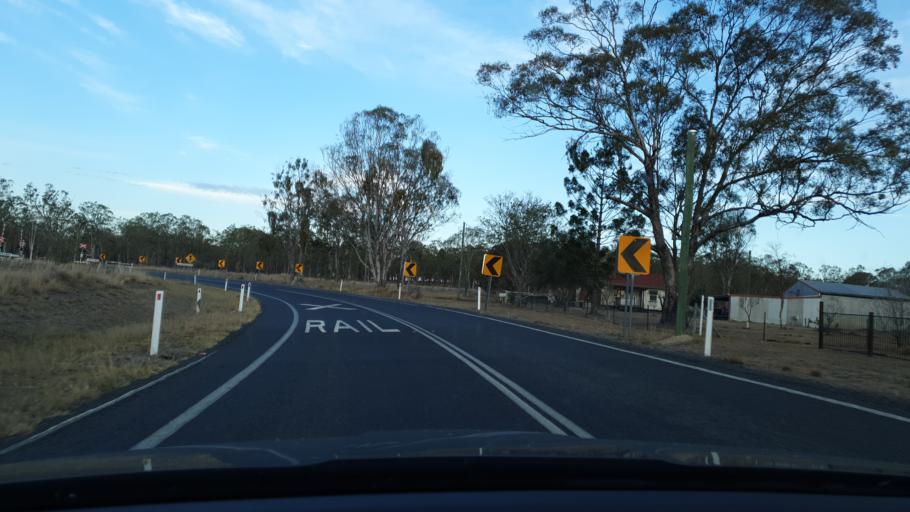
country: AU
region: Queensland
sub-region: Southern Downs
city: Warwick
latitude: -28.1083
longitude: 151.9596
